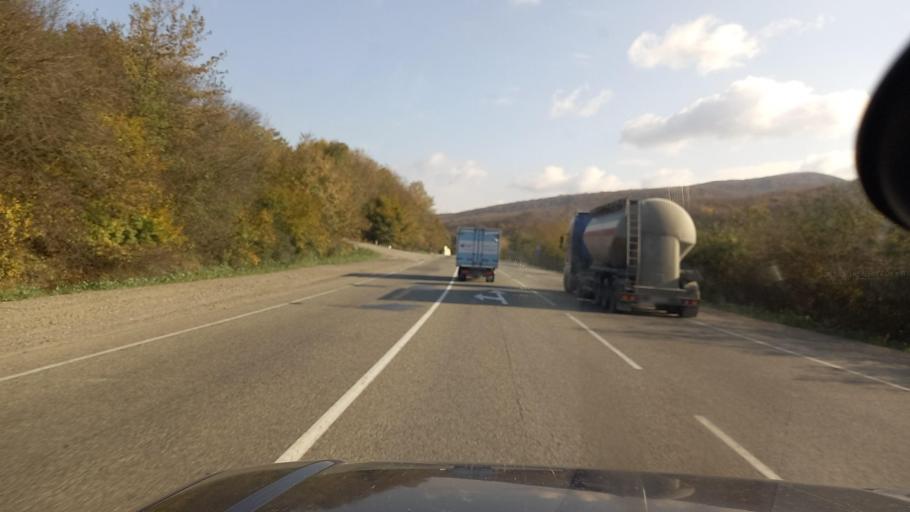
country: RU
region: Krasnodarskiy
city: Verkhnebakanskiy
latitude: 44.8423
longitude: 37.7128
